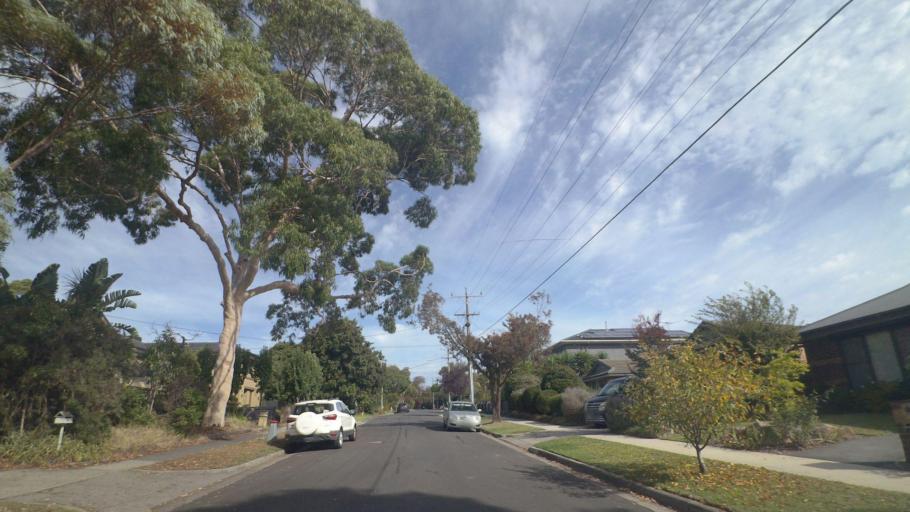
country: AU
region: Victoria
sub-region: Whitehorse
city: Blackburn
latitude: -37.8296
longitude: 145.1421
